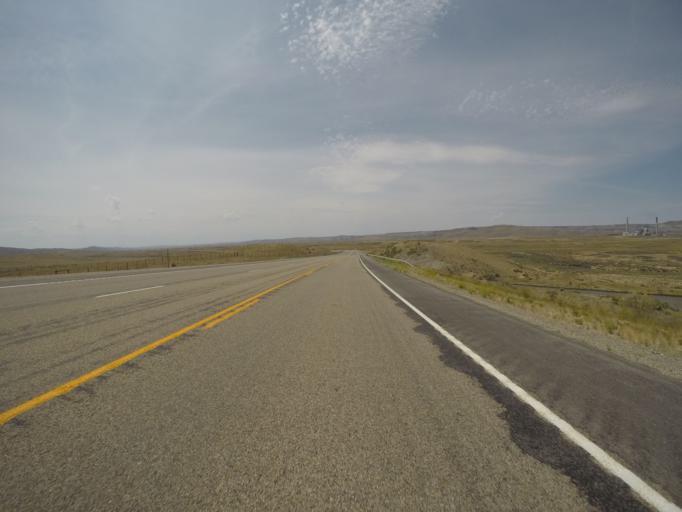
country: US
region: Wyoming
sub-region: Lincoln County
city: Kemmerer
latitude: 41.7567
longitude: -110.5614
